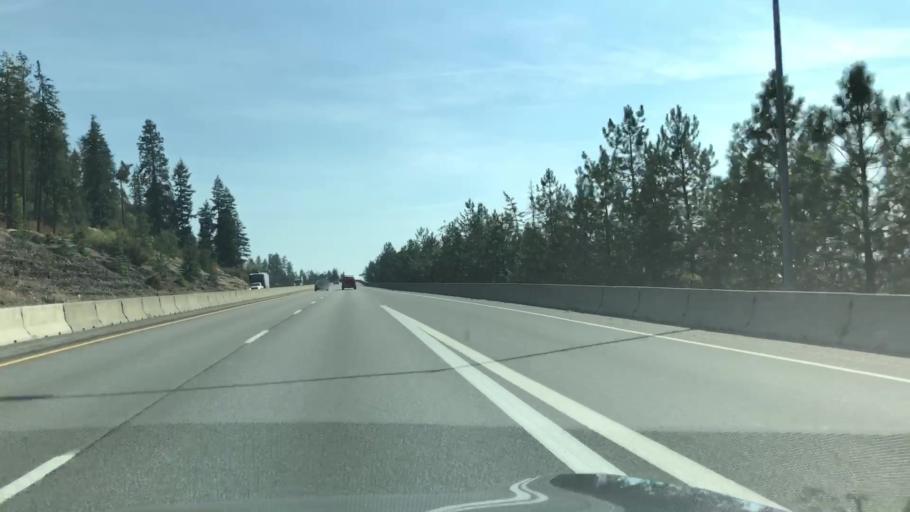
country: US
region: Idaho
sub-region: Kootenai County
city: Coeur d'Alene
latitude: 47.6694
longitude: -116.7509
